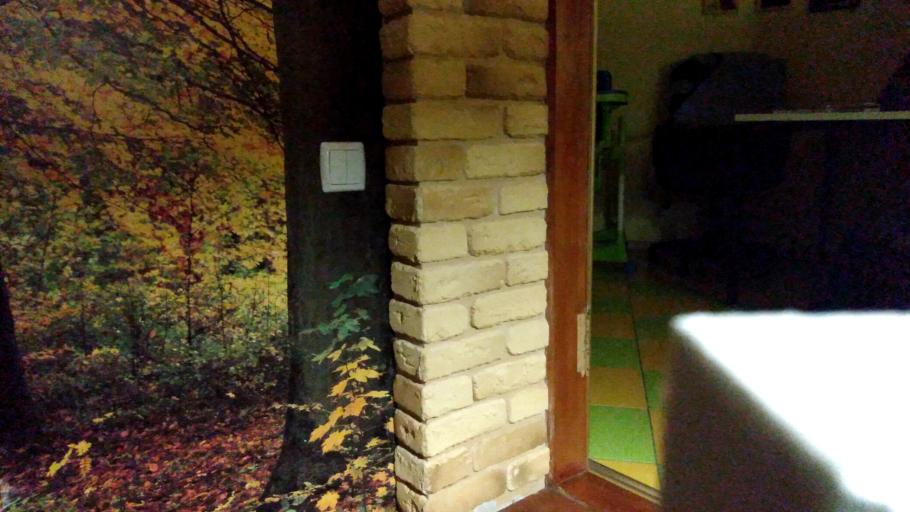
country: RU
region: Vologda
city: Lipin Bor
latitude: 61.0202
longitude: 37.9535
